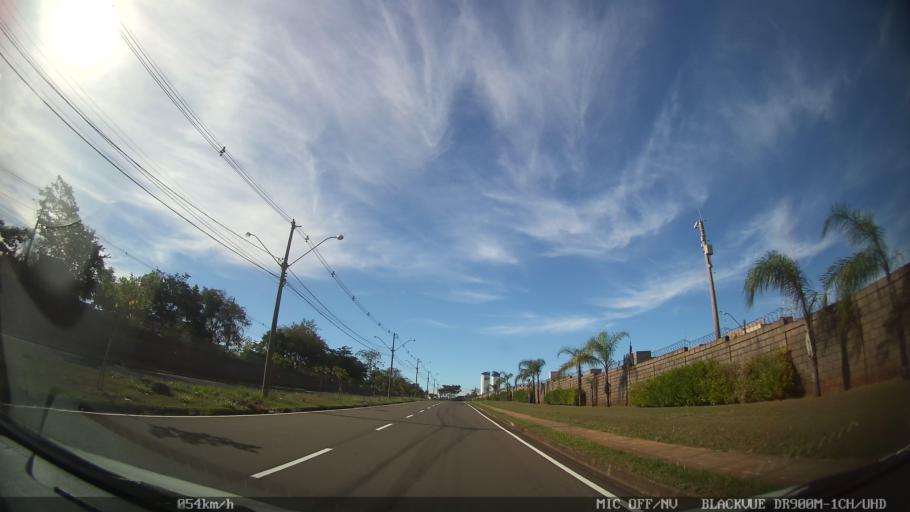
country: BR
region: Sao Paulo
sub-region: Sao Jose Do Rio Preto
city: Sao Jose do Rio Preto
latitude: -20.8089
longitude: -49.3339
